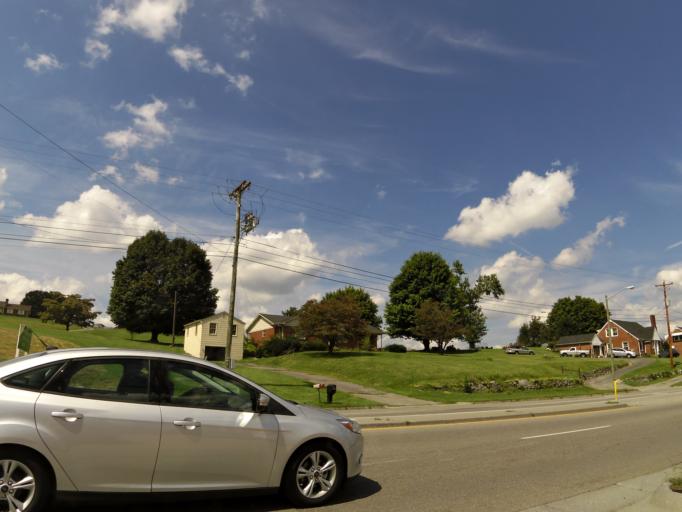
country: US
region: Virginia
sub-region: Washington County
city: Abingdon
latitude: 36.6992
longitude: -82.0086
